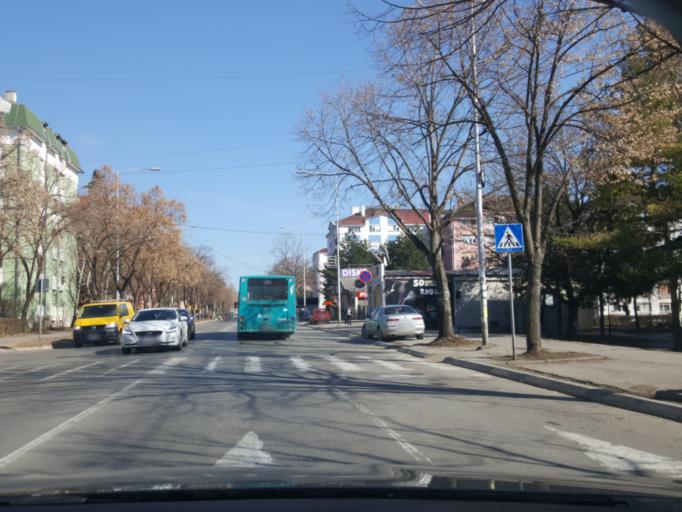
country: RS
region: Central Serbia
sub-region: Nisavski Okrug
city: Nis
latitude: 43.3296
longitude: 21.9313
